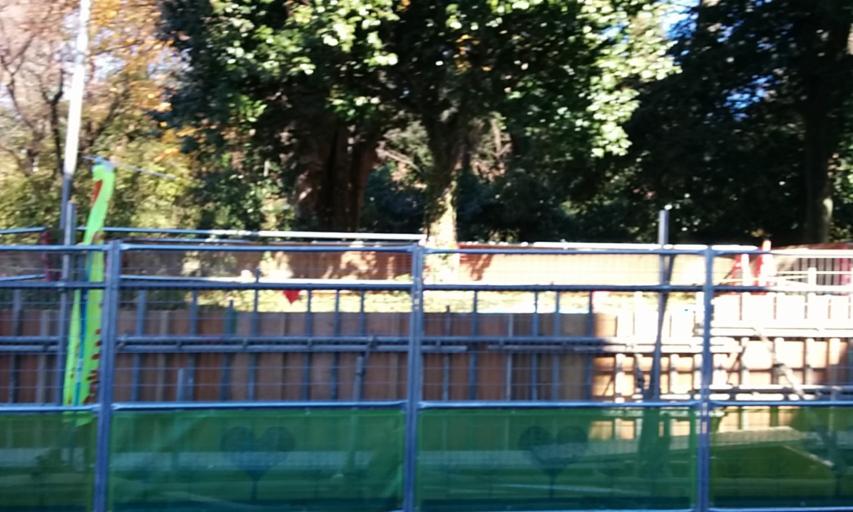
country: JP
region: Tokyo
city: Tokyo
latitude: 35.7177
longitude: 139.7459
